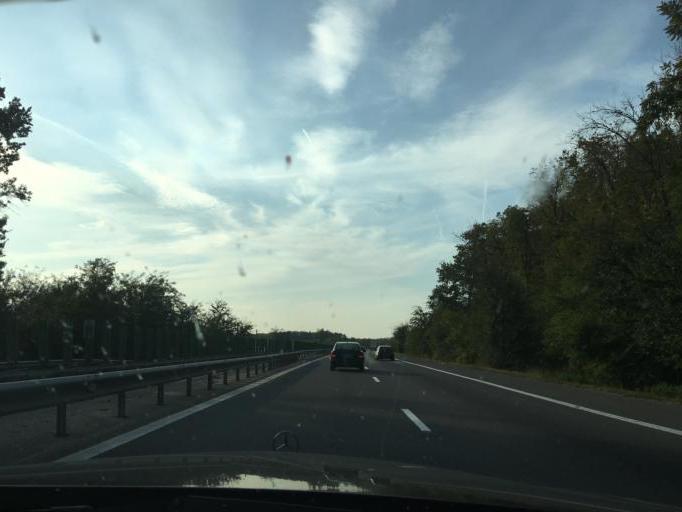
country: RO
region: Calarasi
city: Lehliu-Gara
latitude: 44.4267
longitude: 26.8507
